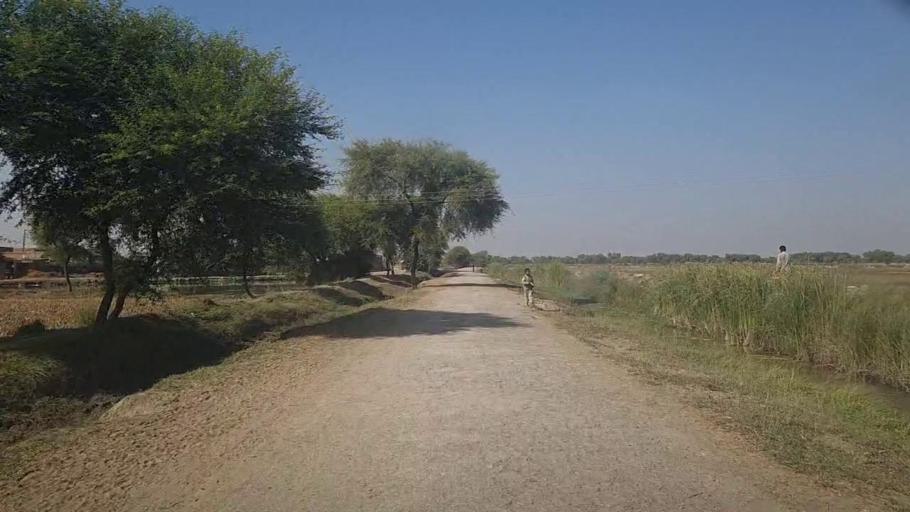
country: PK
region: Sindh
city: Thul
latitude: 28.3108
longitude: 68.7682
